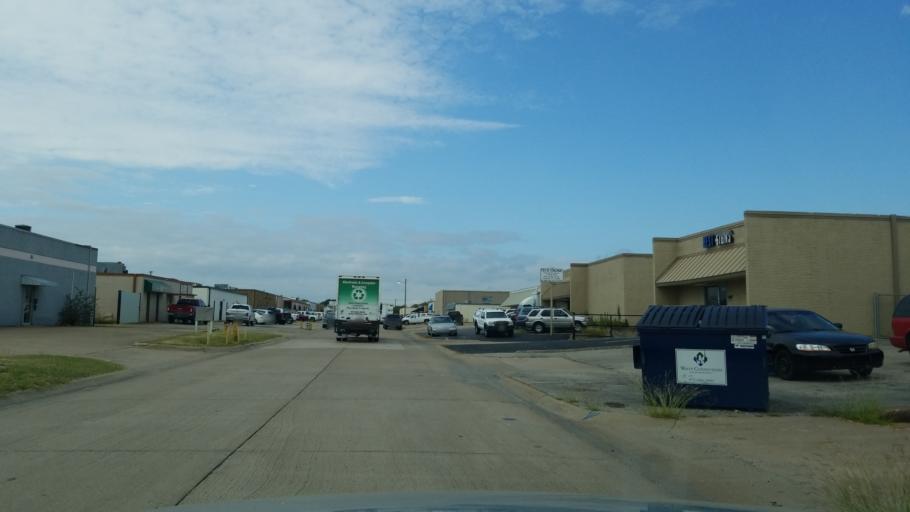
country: US
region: Texas
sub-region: Dallas County
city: Garland
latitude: 32.8988
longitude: -96.6875
